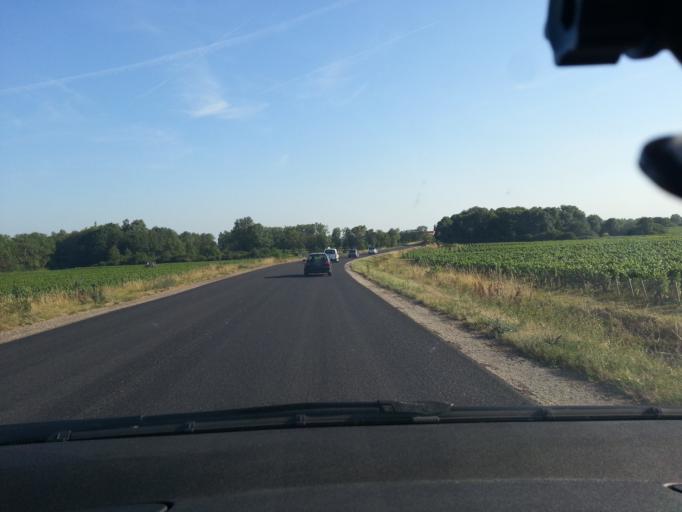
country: FR
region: Bourgogne
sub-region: Departement de la Cote-d'Or
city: Meursault
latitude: 46.9905
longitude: 4.7935
